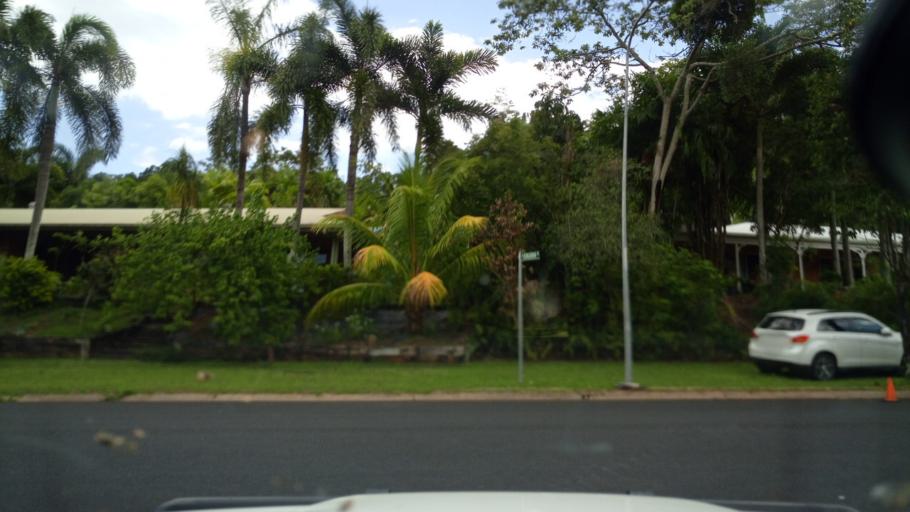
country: AU
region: Queensland
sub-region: Cairns
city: Redlynch
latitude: -16.9073
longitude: 145.7168
